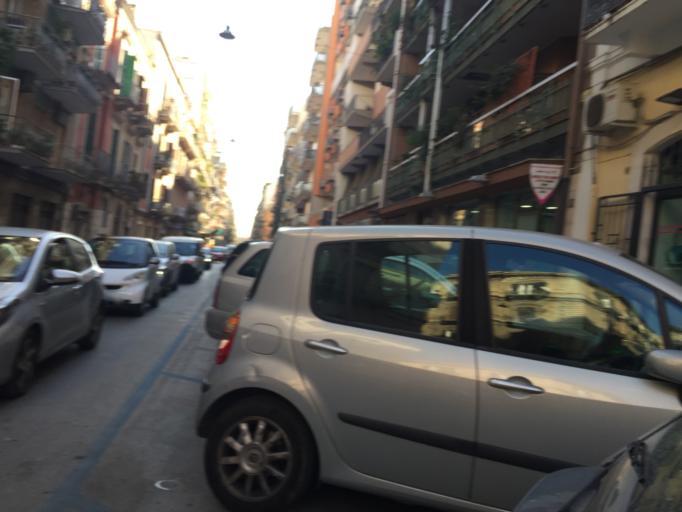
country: IT
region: Apulia
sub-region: Provincia di Bari
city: Bari
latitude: 41.1234
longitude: 16.8610
